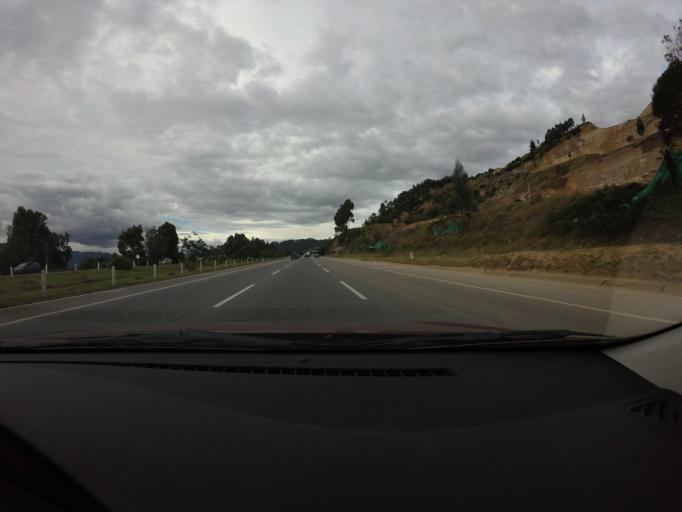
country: CO
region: Cundinamarca
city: Cajica
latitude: 4.9262
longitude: -73.9958
